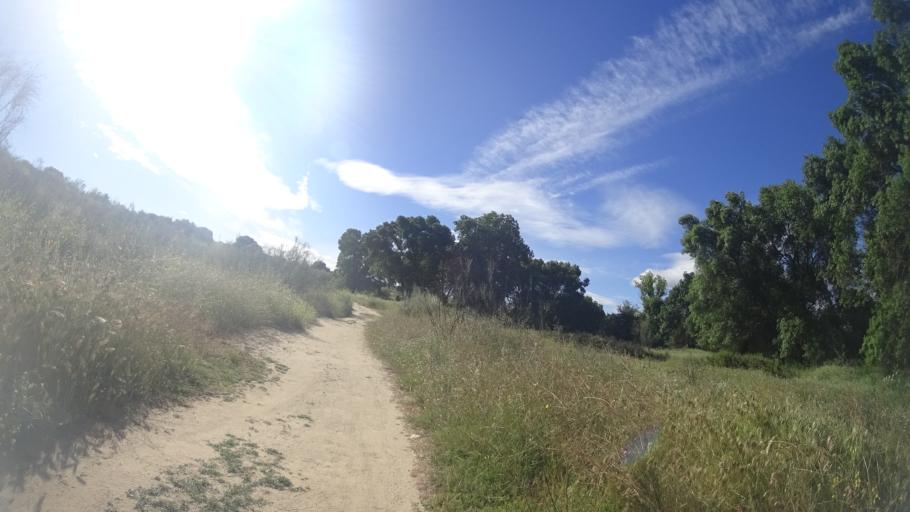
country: ES
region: Madrid
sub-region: Provincia de Madrid
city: Villanueva del Pardillo
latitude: 40.5142
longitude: -3.9407
